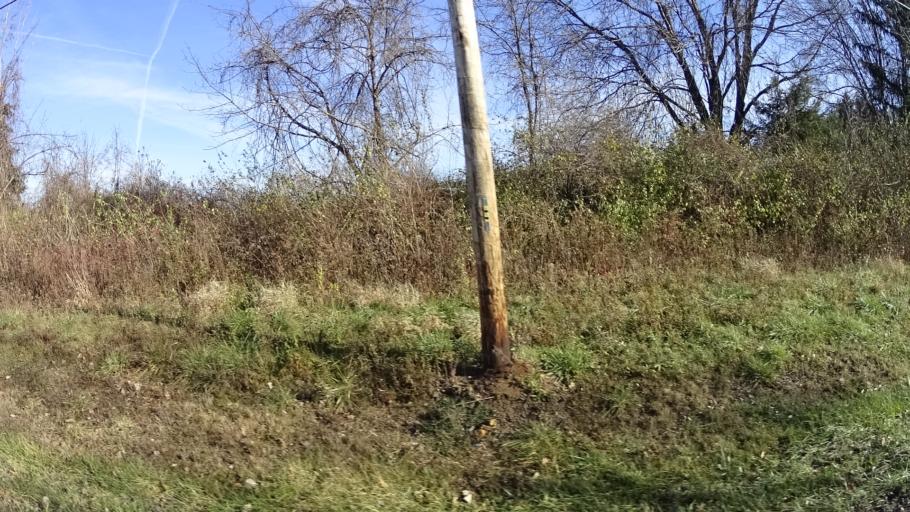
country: US
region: Ohio
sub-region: Lorain County
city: Wellington
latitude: 41.1096
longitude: -82.2392
